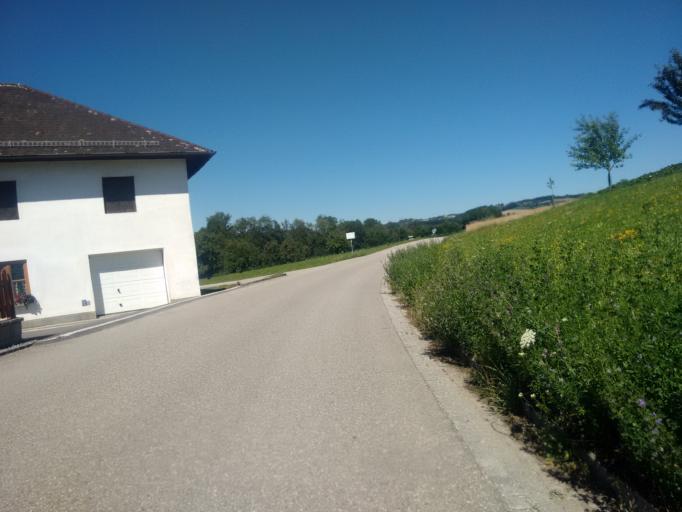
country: AT
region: Upper Austria
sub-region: Wels-Land
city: Buchkirchen
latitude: 48.2273
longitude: 13.9771
